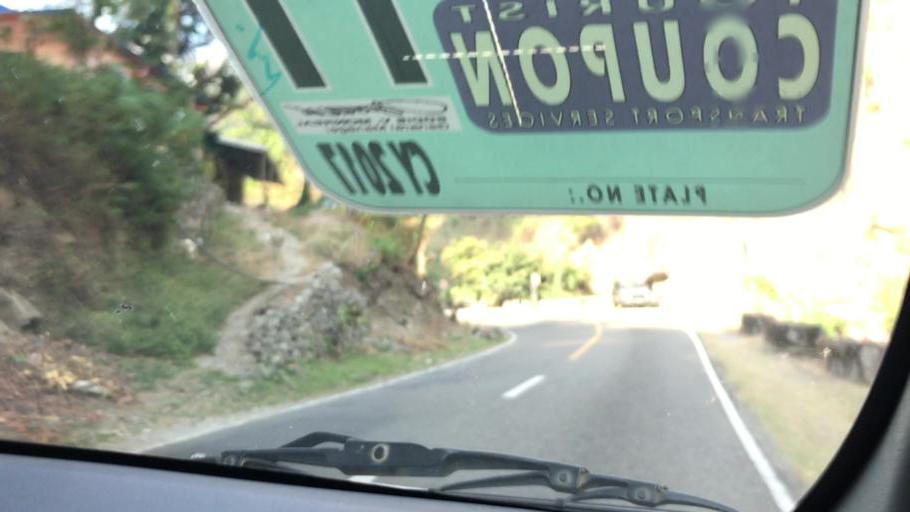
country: PH
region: Cordillera
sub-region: Province of Benguet
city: Tuba
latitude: 16.3221
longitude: 120.6152
